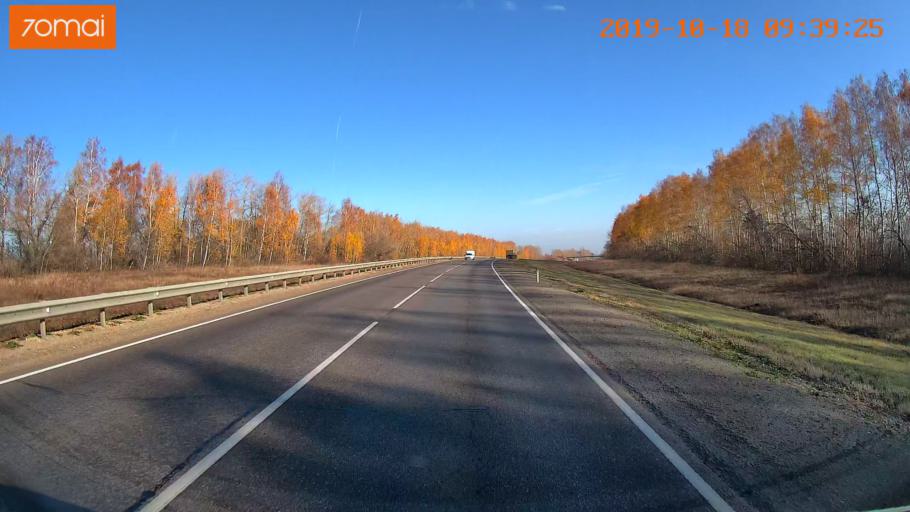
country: RU
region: Tula
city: Yefremov
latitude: 53.2529
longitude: 38.1352
